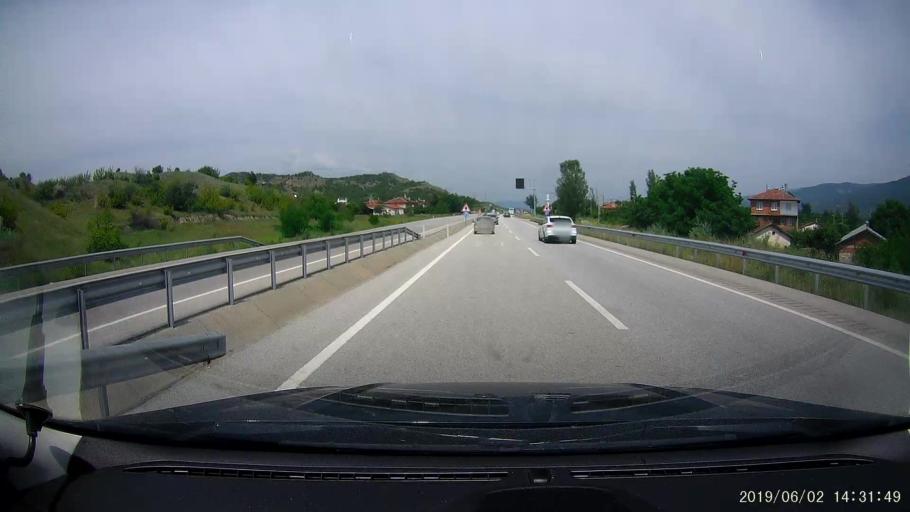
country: TR
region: Kastamonu
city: Tosya
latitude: 41.0222
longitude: 34.1441
